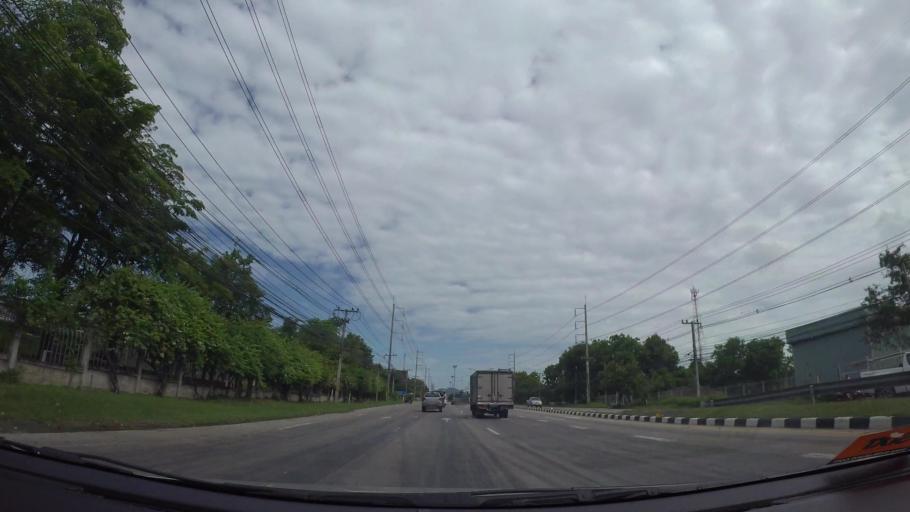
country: TH
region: Rayong
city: Ban Chang
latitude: 12.7206
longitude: 101.1558
